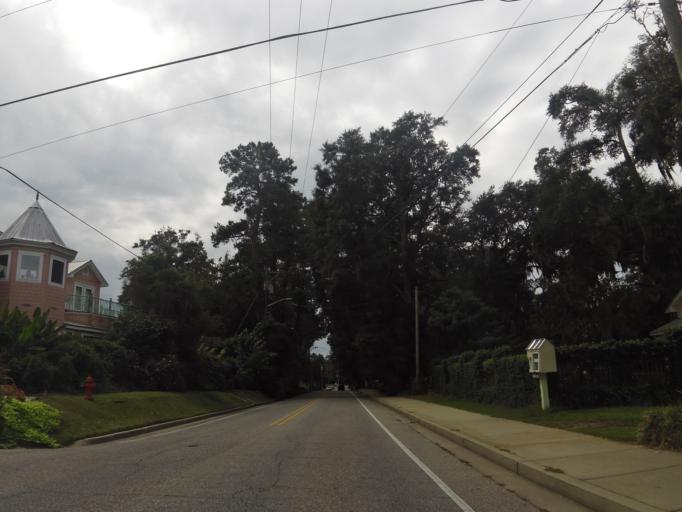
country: US
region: Alabama
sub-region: Baldwin County
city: Fairhope
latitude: 30.5200
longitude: -87.9134
